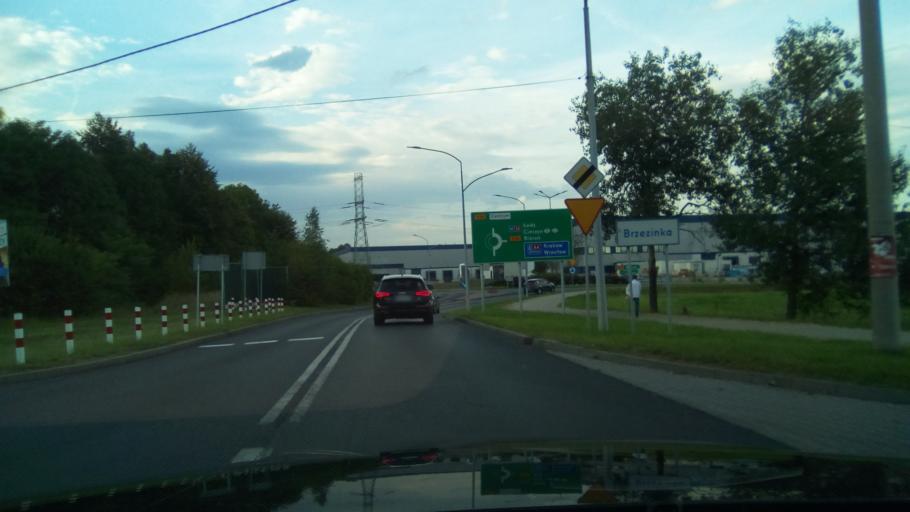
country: PL
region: Silesian Voivodeship
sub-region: Myslowice
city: Myslowice
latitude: 50.1930
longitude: 19.1630
